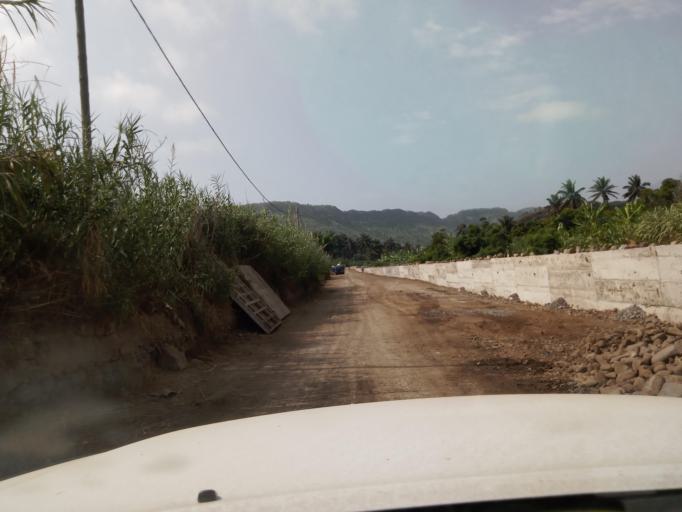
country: CV
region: Santa Cruz
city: Pedra Badejo
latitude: 15.1230
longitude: -23.5464
